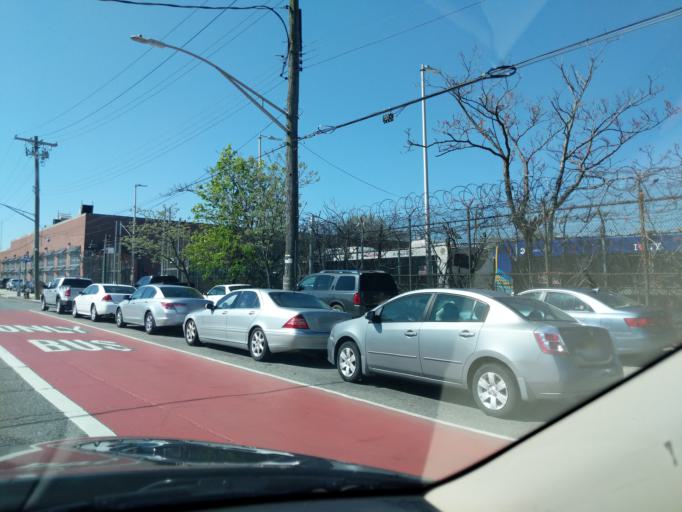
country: US
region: New York
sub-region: Kings County
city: Brooklyn
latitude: 40.6173
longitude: -73.9266
